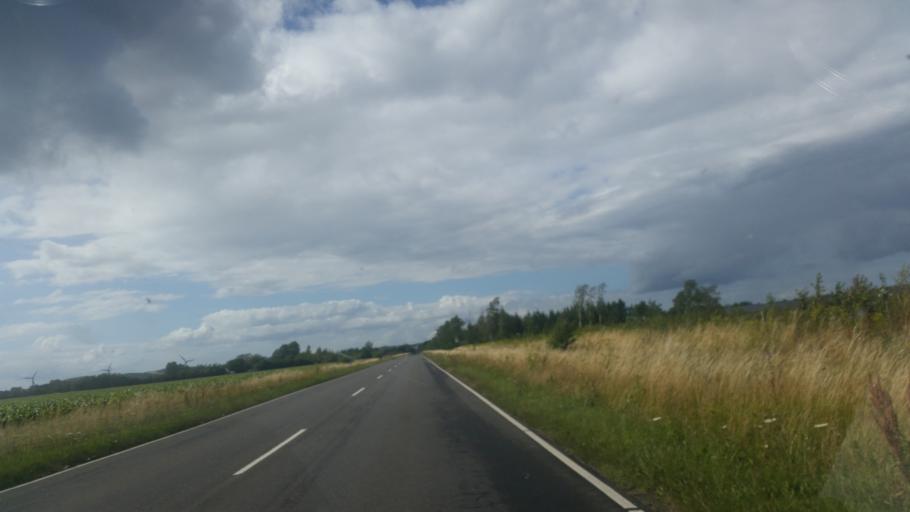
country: DK
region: Zealand
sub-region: Odsherred Kommune
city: Asnaes
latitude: 55.7615
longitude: 11.5067
